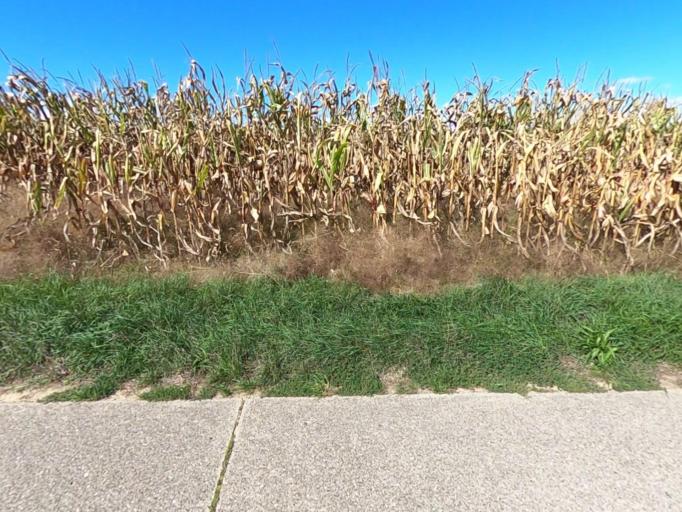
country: DE
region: Baden-Wuerttemberg
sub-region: Freiburg Region
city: Fischingen
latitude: 47.6886
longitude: 7.6143
